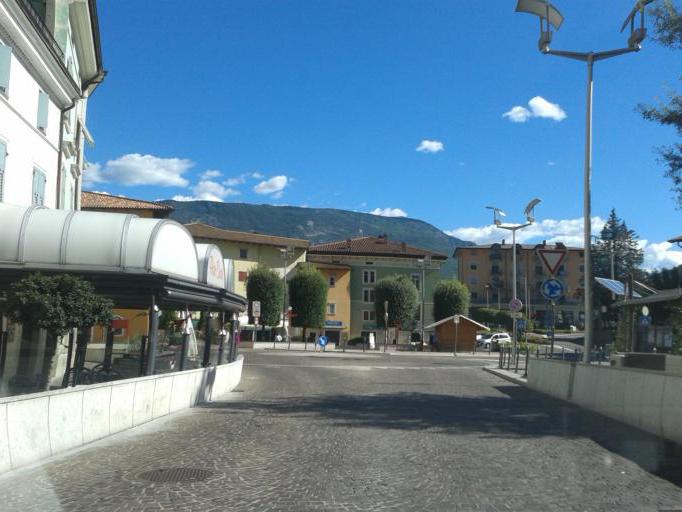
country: IT
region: Trentino-Alto Adige
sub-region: Provincia di Trento
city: Mori
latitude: 45.8522
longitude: 10.9774
